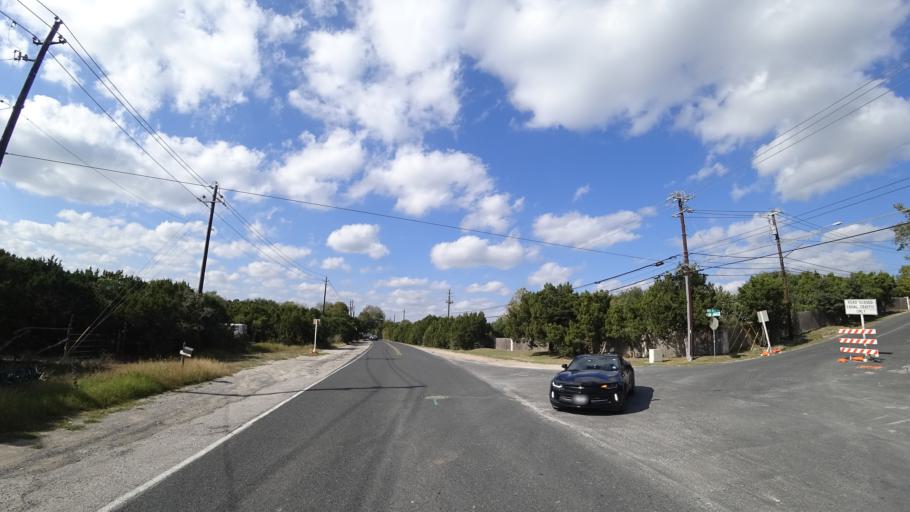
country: US
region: Texas
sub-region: Travis County
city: Barton Creek
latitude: 30.2471
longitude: -97.8829
